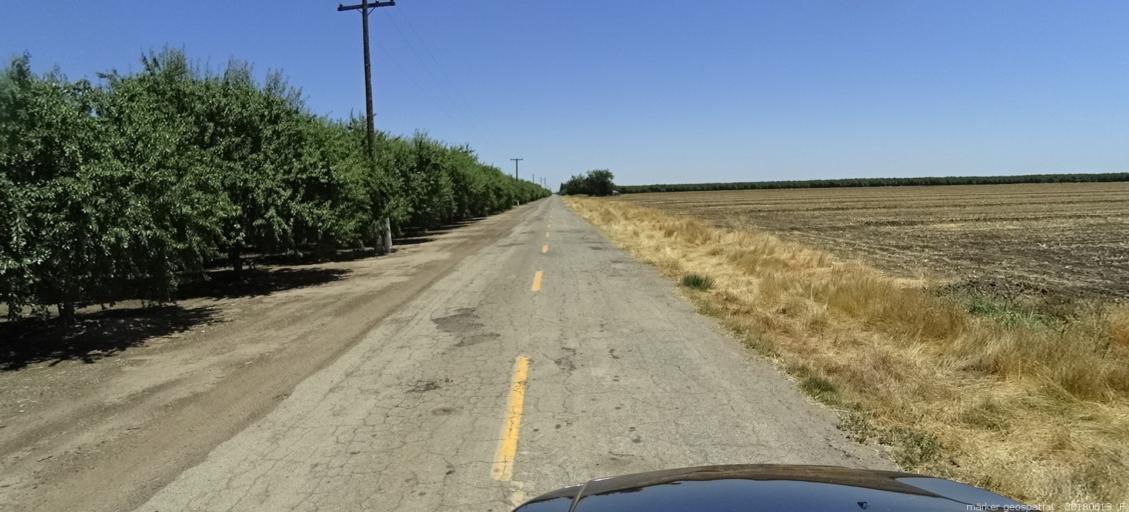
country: US
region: California
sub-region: Madera County
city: Chowchilla
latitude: 37.0327
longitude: -120.2915
